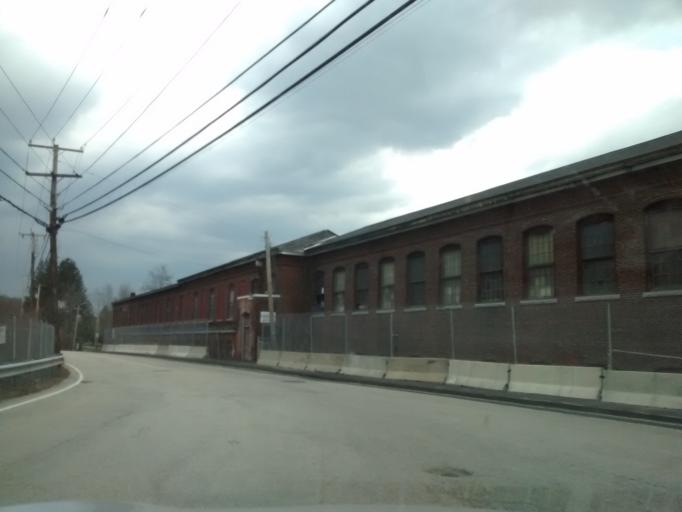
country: US
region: Massachusetts
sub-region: Worcester County
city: Millbury
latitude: 42.1757
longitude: -71.7750
